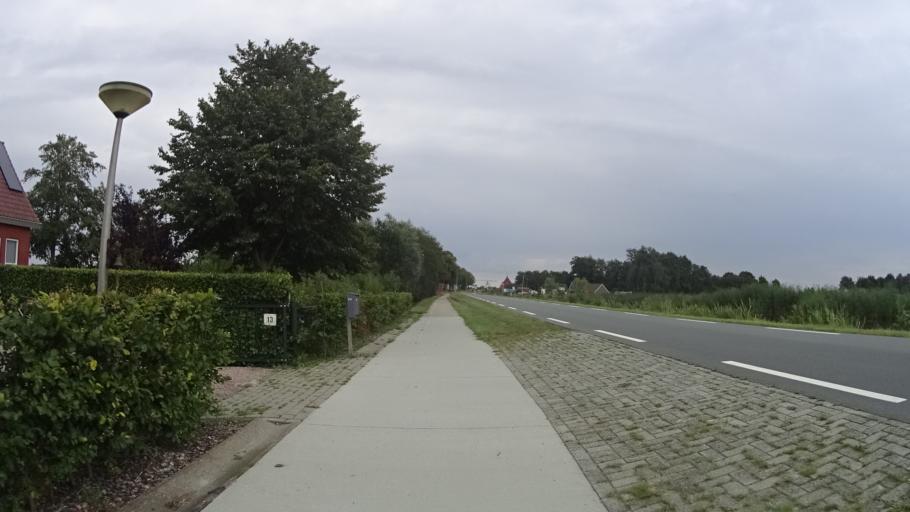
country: NL
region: Groningen
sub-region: Gemeente Hoogezand-Sappemeer
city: Hoogezand
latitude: 53.2355
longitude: 6.7076
